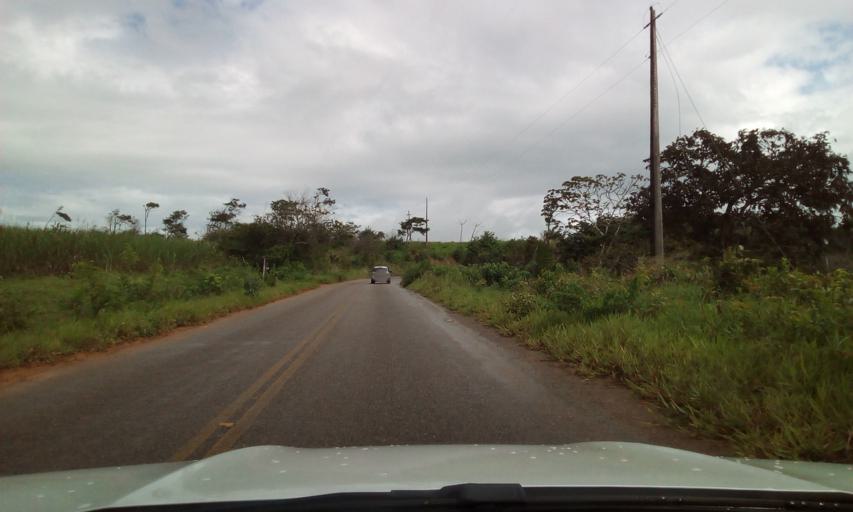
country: BR
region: Paraiba
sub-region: Areia
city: Areia
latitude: -6.9583
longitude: -35.6733
